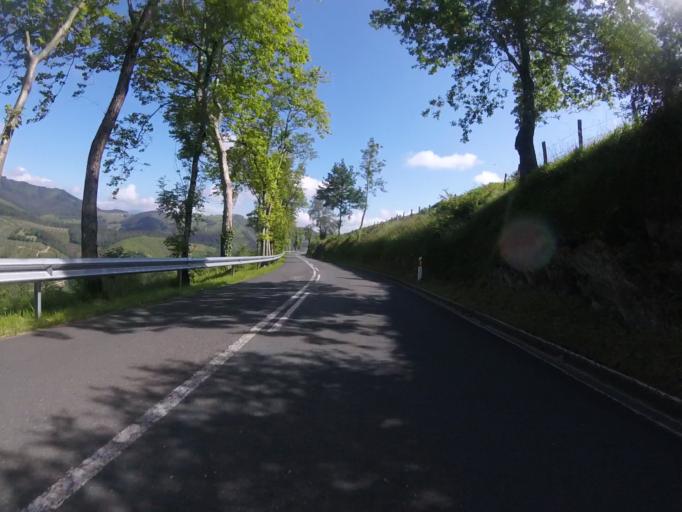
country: ES
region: Basque Country
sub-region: Provincia de Guipuzcoa
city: Ormaiztegui
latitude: 43.0905
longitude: -2.2432
